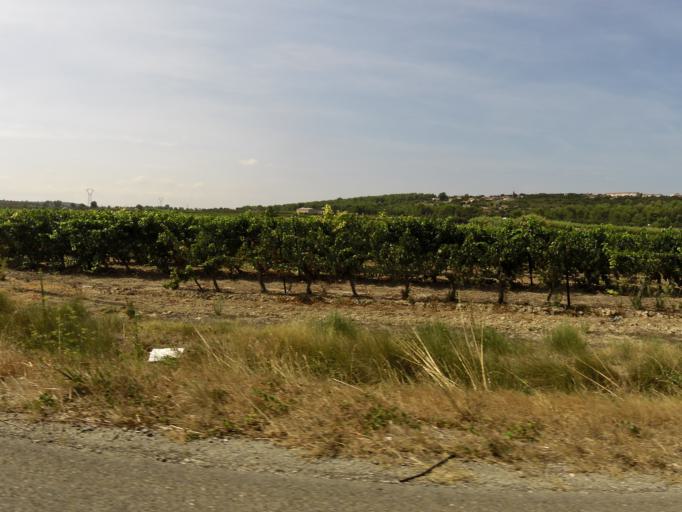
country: FR
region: Languedoc-Roussillon
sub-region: Departement du Gard
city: Mus
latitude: 43.7571
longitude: 4.2045
